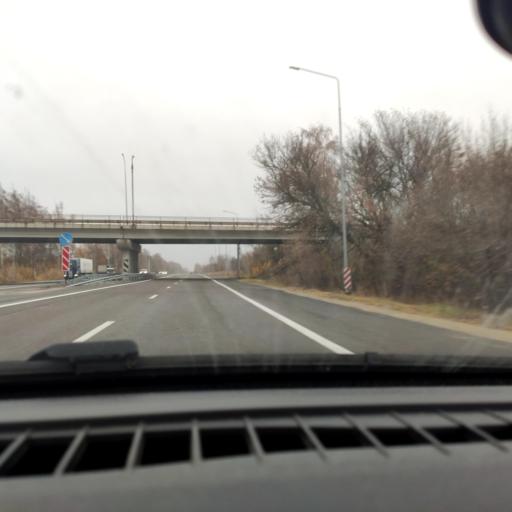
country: RU
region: Voronezj
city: Kolodeznyy
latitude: 51.3386
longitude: 39.0240
